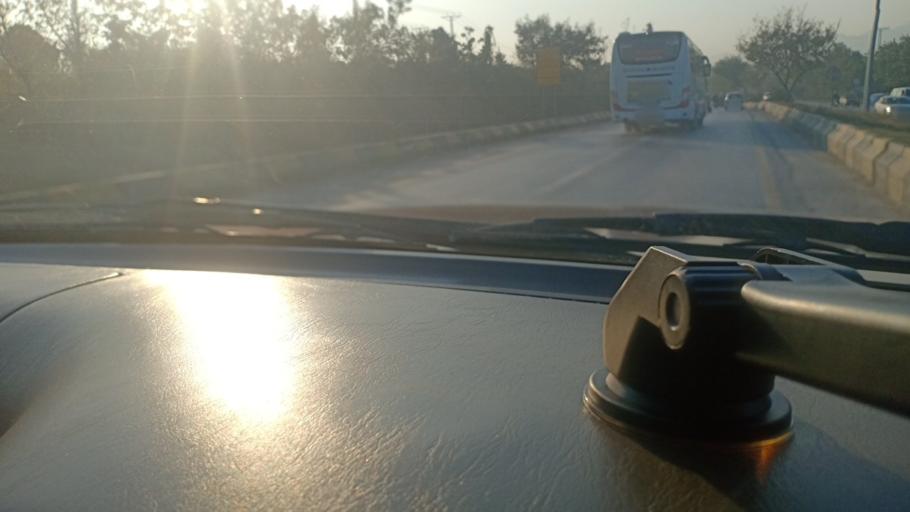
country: PK
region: Islamabad
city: Islamabad
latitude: 33.7347
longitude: 73.1613
